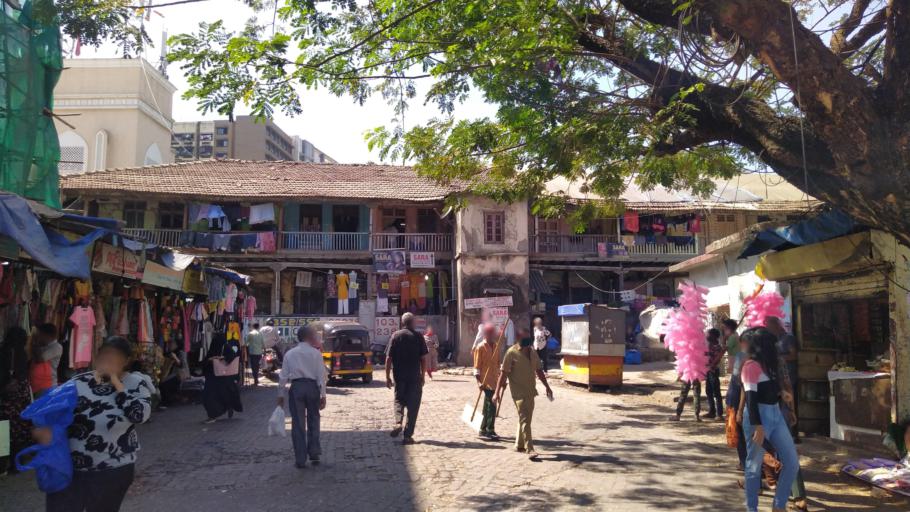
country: IN
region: Maharashtra
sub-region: Mumbai Suburban
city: Mumbai
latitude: 19.0701
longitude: 72.8781
